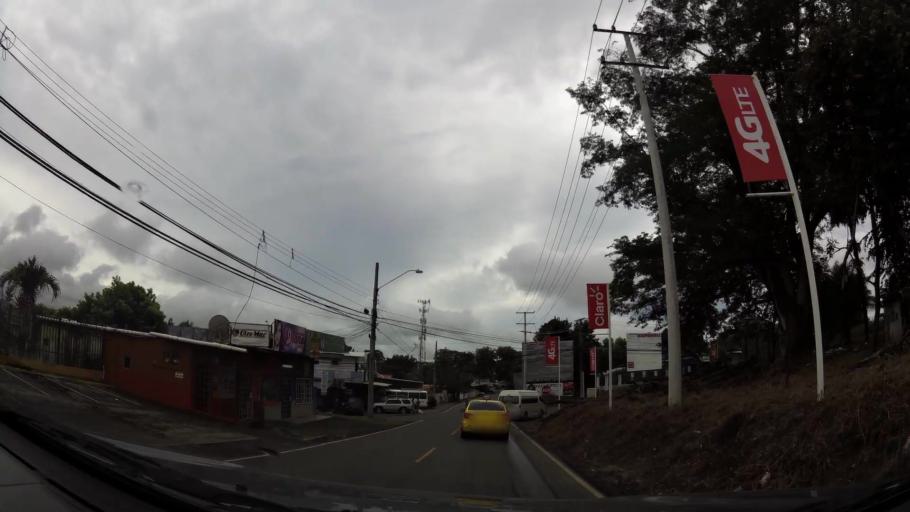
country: PA
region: Chiriqui
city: David
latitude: 8.4358
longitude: -82.4211
